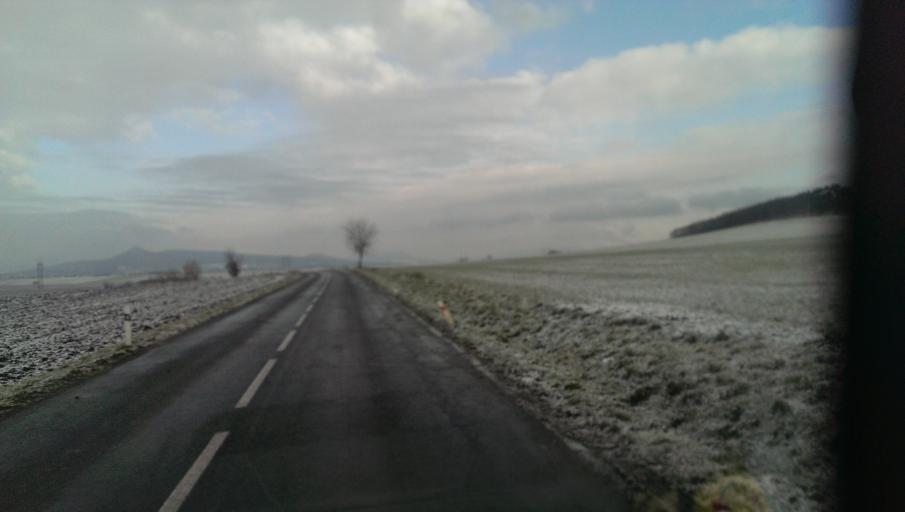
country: CZ
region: Ustecky
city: Trebenice
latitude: 50.4408
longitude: 14.0010
